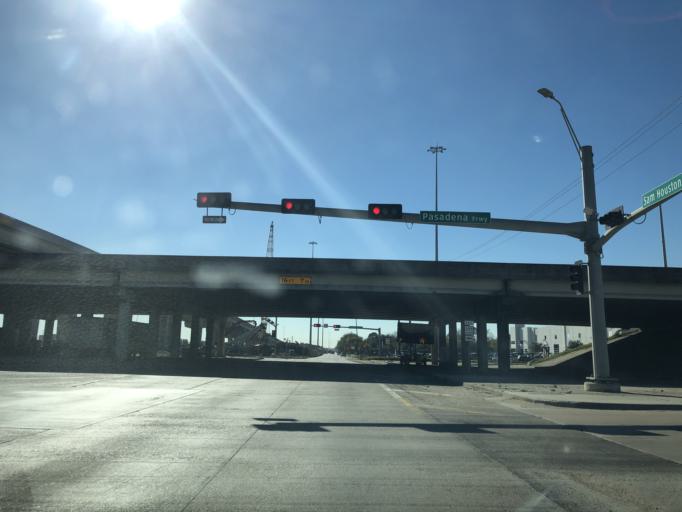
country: US
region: Texas
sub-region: Harris County
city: Deer Park
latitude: 29.7125
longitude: -95.1538
